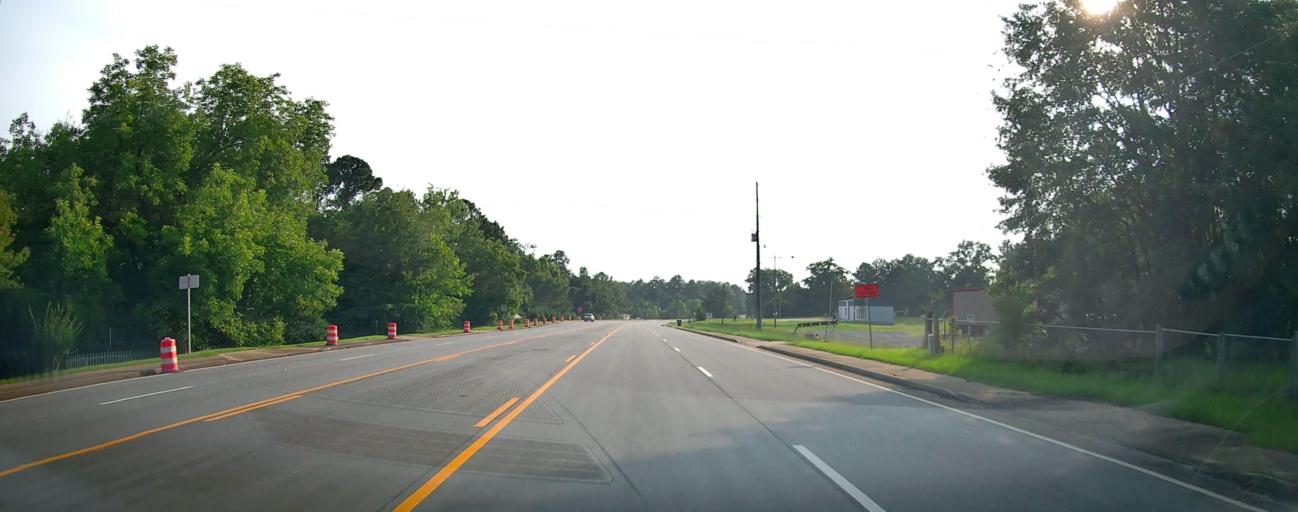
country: US
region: Georgia
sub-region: Talbot County
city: Talbotton
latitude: 32.5764
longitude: -84.5577
